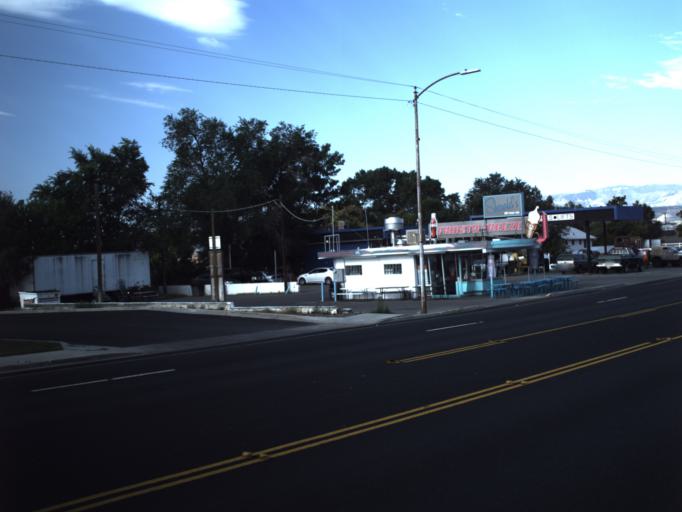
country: US
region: Utah
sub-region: Carbon County
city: Price
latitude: 39.5996
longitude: -110.8023
